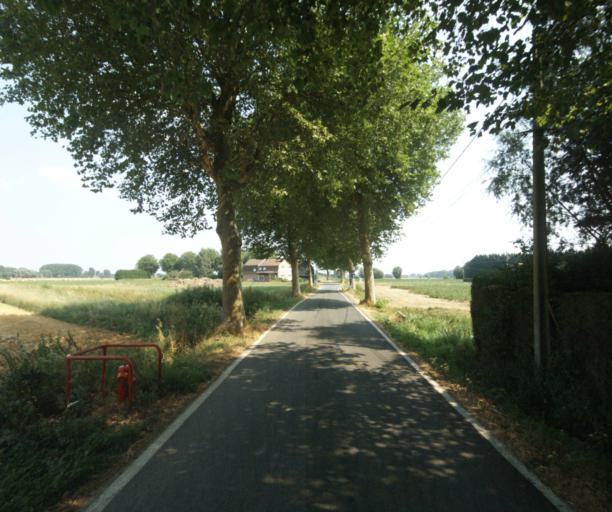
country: FR
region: Nord-Pas-de-Calais
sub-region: Departement du Nord
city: Quesnoy-sur-Deule
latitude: 50.7245
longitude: 3.0391
